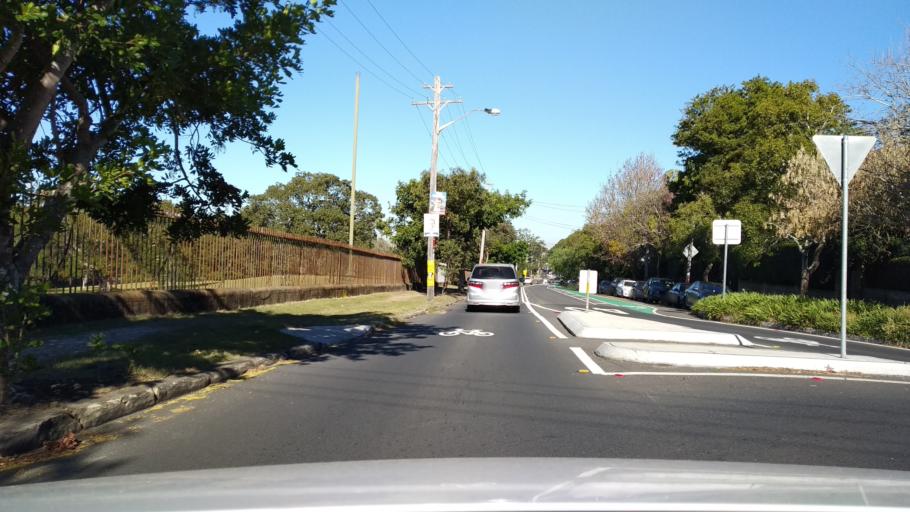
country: AU
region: New South Wales
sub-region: Woollahra
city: Woollahra
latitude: -33.8922
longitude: 151.2322
